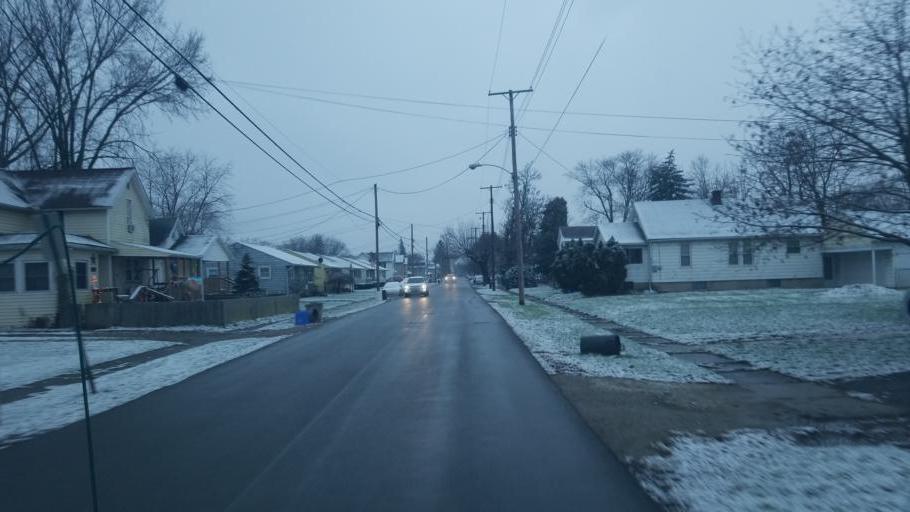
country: US
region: Ohio
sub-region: Marion County
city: Marion
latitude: 40.5951
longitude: -83.1160
